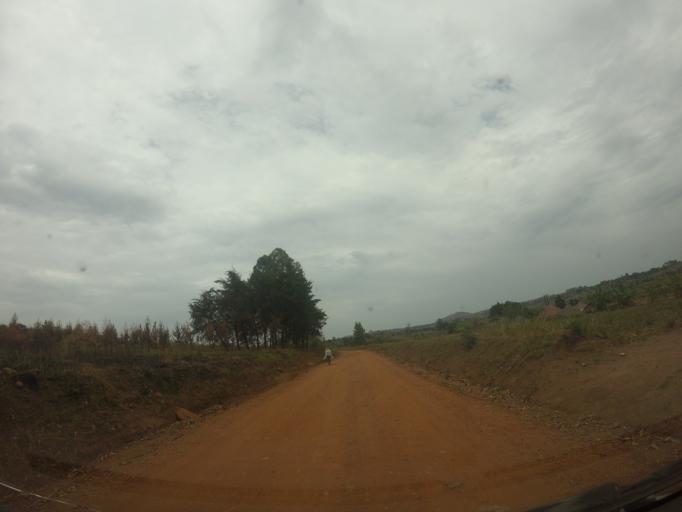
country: UG
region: Northern Region
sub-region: Arua District
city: Arua
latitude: 2.8463
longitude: 30.8889
